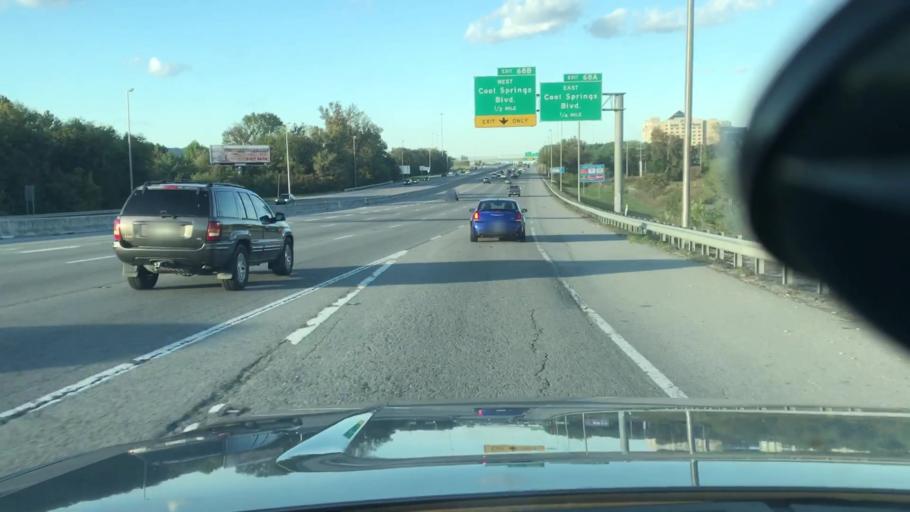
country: US
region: Tennessee
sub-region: Williamson County
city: Franklin
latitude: 35.9387
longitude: -86.8170
